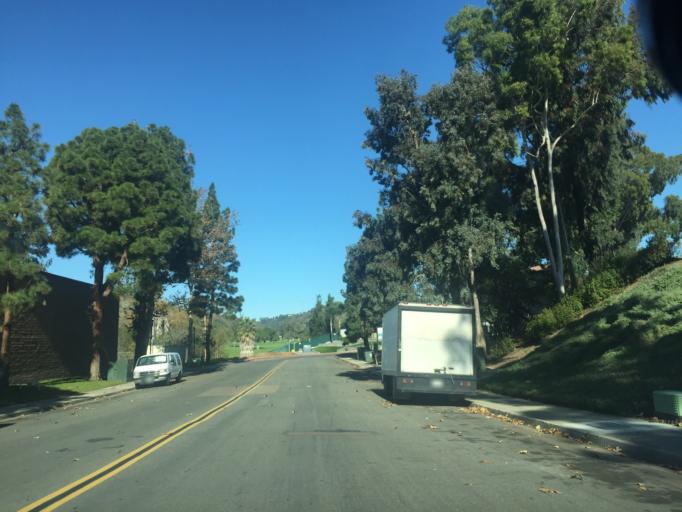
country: US
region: California
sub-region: San Diego County
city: La Mesa
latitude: 32.7920
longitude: -117.0996
